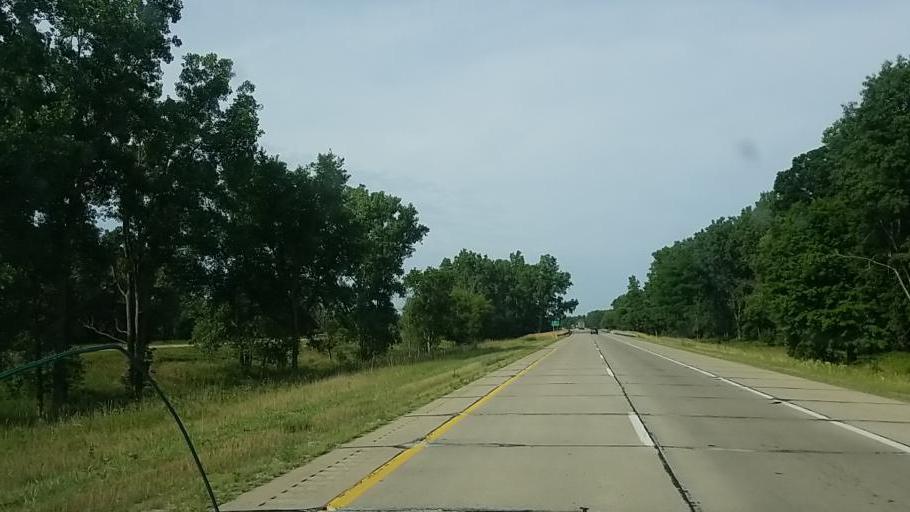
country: US
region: Michigan
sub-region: Eaton County
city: Olivet
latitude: 42.4741
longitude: -84.8895
